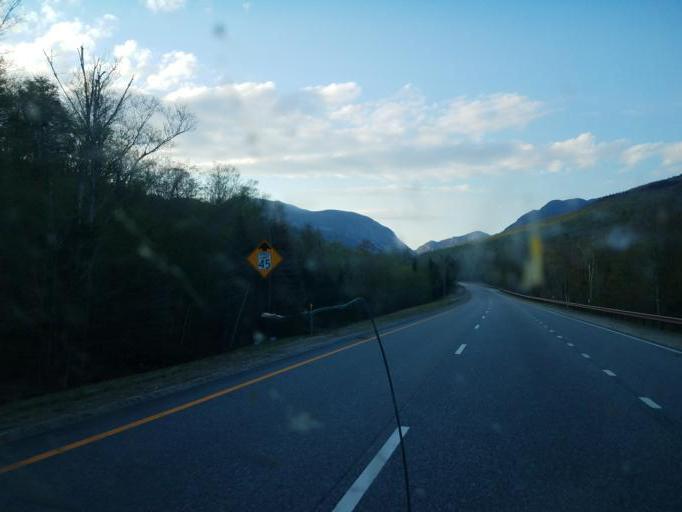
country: US
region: New Hampshire
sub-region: Grafton County
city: Woodstock
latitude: 44.1086
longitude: -71.6825
